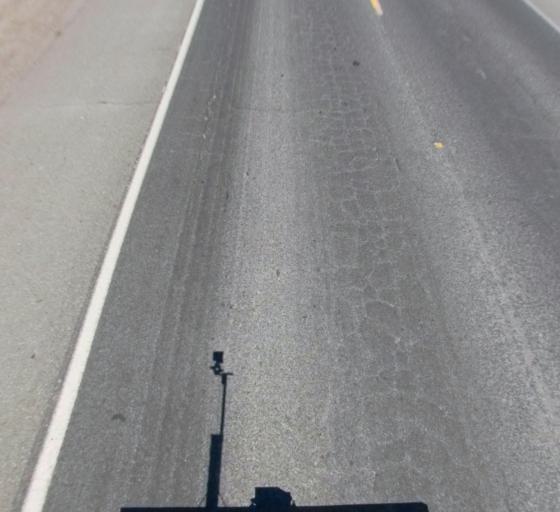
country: US
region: California
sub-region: Madera County
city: Parkwood
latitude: 36.9238
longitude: -120.0485
